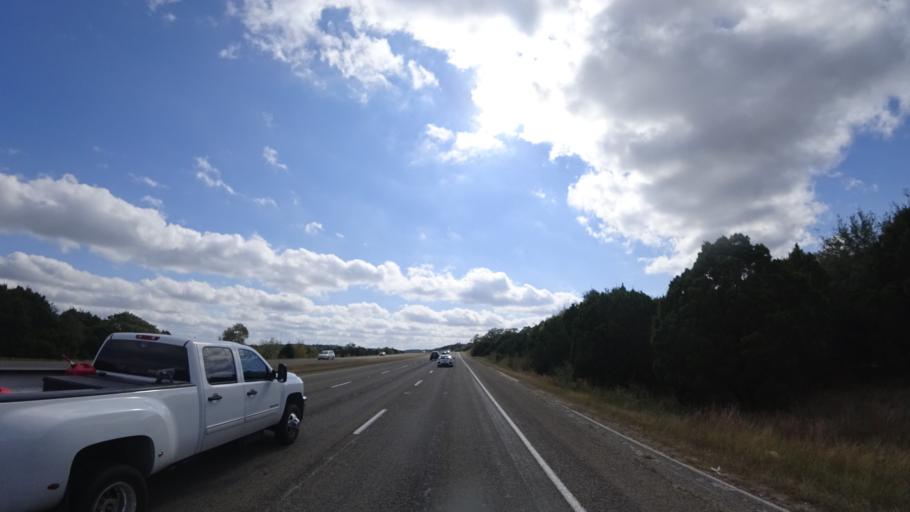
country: US
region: Texas
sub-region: Travis County
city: Barton Creek
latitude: 30.2740
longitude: -97.8977
